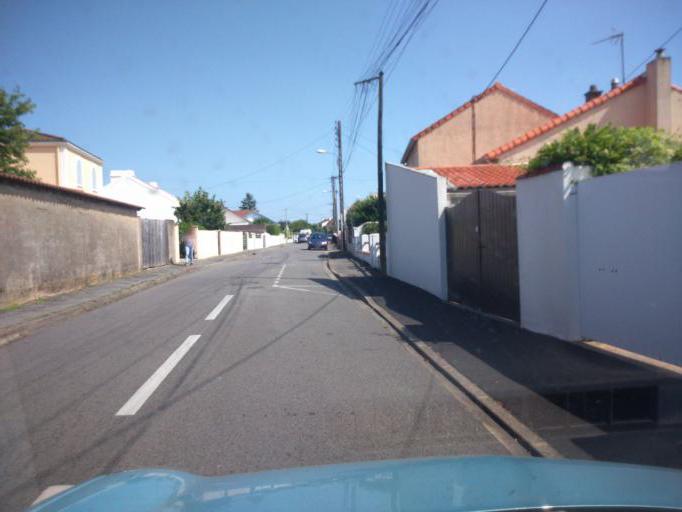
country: FR
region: Pays de la Loire
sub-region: Departement de la Loire-Atlantique
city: Saint-Sebastien-sur-Loire
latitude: 47.2008
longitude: -1.5167
